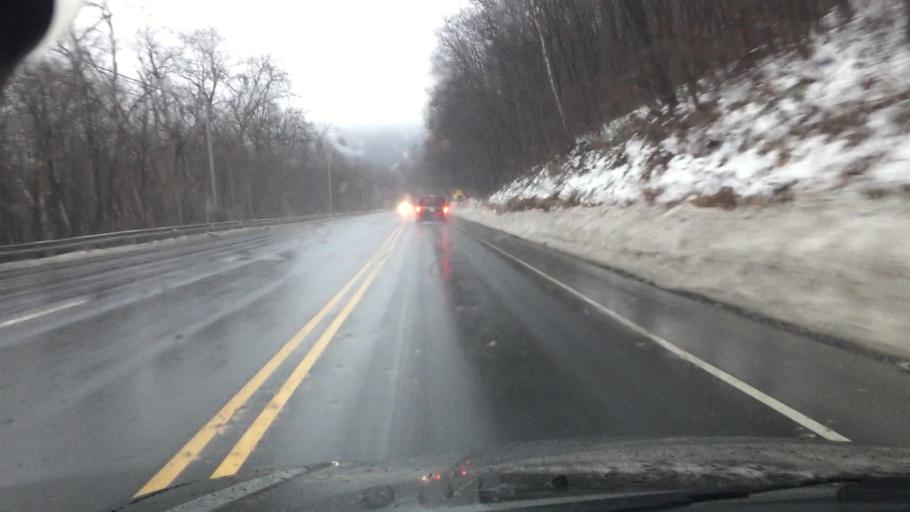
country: US
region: Pennsylvania
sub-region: Luzerne County
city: Harleigh
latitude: 41.0030
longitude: -75.9772
